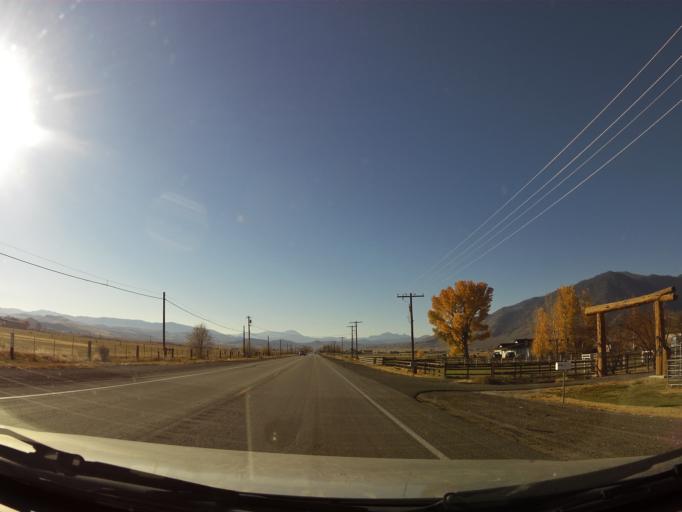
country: US
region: Nevada
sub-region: Douglas County
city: Gardnerville Ranchos
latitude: 38.8864
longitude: -119.7792
